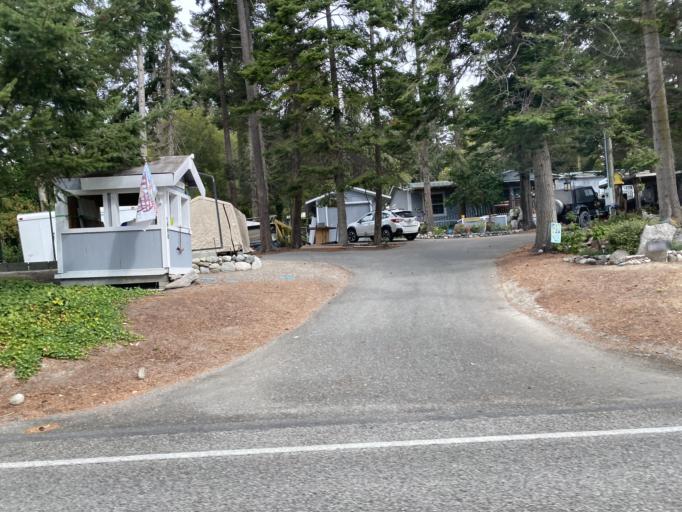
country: US
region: Washington
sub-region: Island County
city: Coupeville
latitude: 48.2395
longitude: -122.7011
